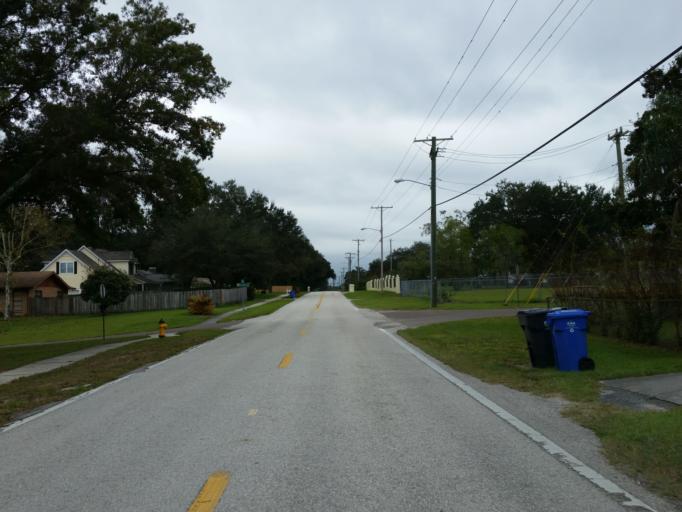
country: US
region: Florida
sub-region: Hillsborough County
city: Bloomingdale
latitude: 27.9083
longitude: -82.2615
